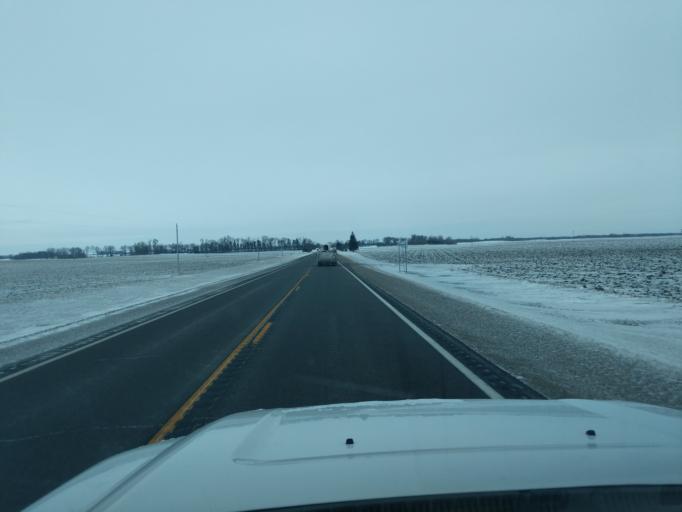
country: US
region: Minnesota
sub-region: Redwood County
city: Redwood Falls
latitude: 44.5964
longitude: -94.9944
